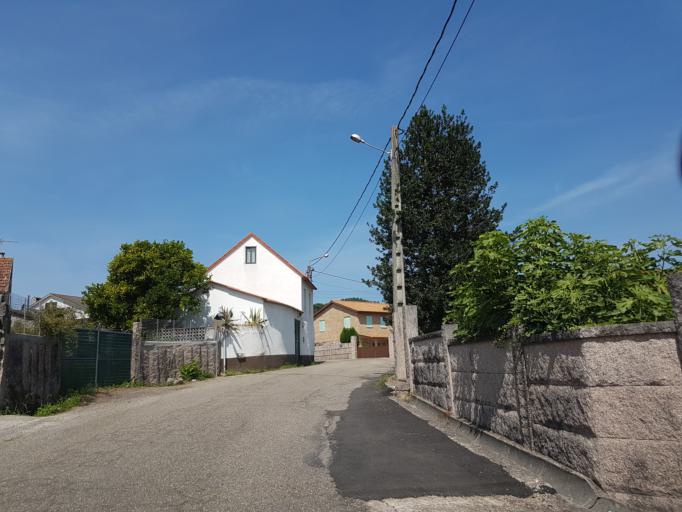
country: ES
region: Galicia
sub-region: Provincia de Pontevedra
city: Porrino
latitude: 42.2142
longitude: -8.6204
